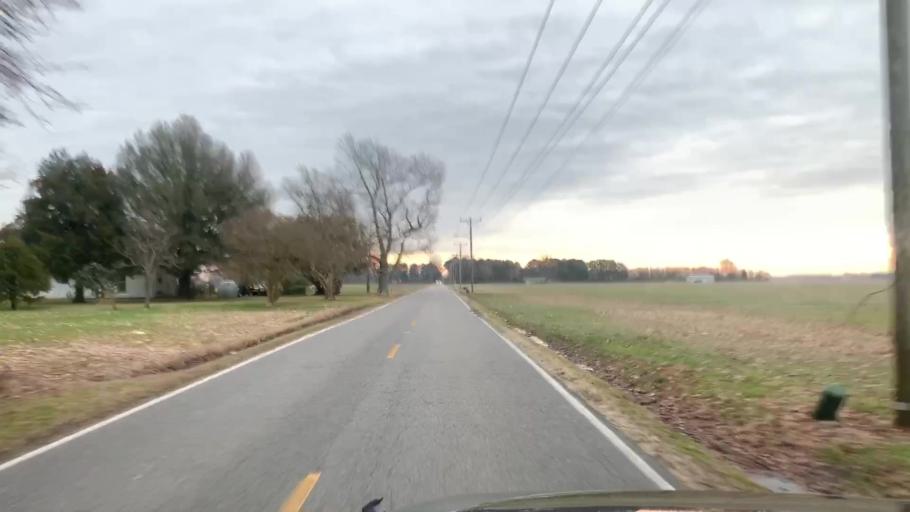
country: US
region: North Carolina
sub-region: Currituck County
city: Moyock
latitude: 36.6344
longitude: -76.1873
